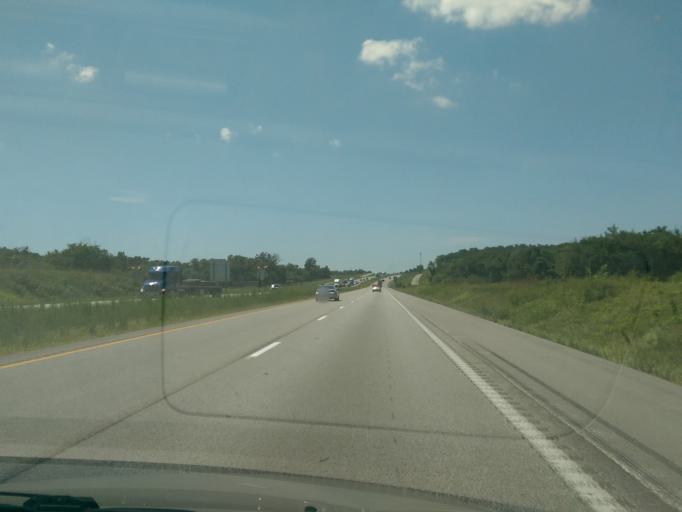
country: US
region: Missouri
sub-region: Saline County
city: Marshall
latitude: 38.9700
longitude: -93.2437
